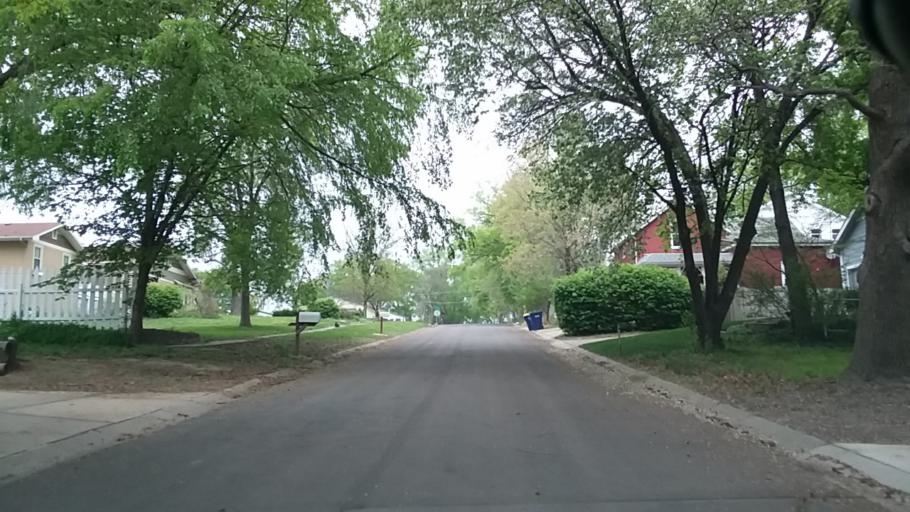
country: US
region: Kansas
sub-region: Douglas County
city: Eudora
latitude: 38.9457
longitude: -95.0978
